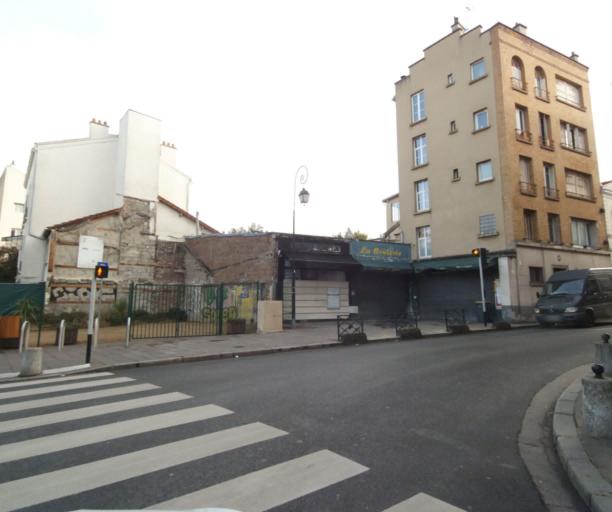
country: FR
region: Ile-de-France
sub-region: Departement des Hauts-de-Seine
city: Nanterre
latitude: 48.8941
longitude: 2.1959
